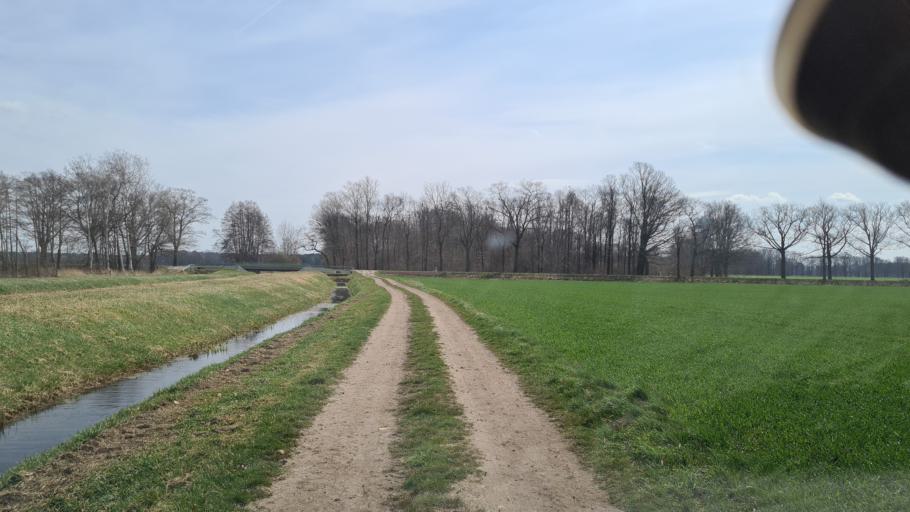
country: DE
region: Brandenburg
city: Bronkow
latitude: 51.6204
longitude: 13.9180
